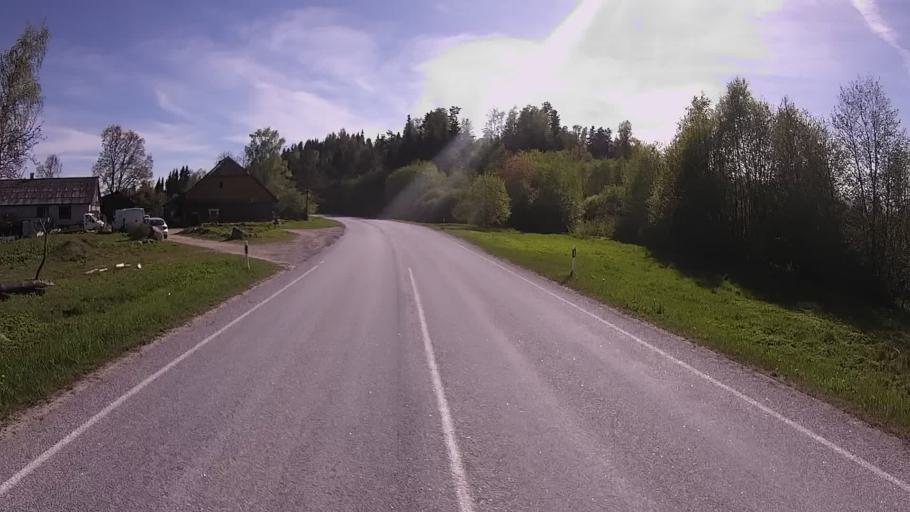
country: EE
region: Vorumaa
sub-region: Antsla vald
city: Vana-Antsla
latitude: 58.0202
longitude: 26.5016
